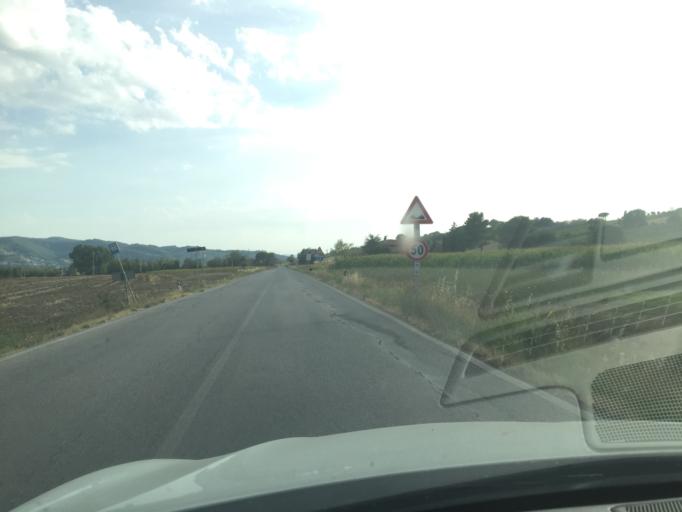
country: IT
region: Umbria
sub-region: Provincia di Perugia
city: Ospedalicchio
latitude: 43.0498
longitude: 12.4893
